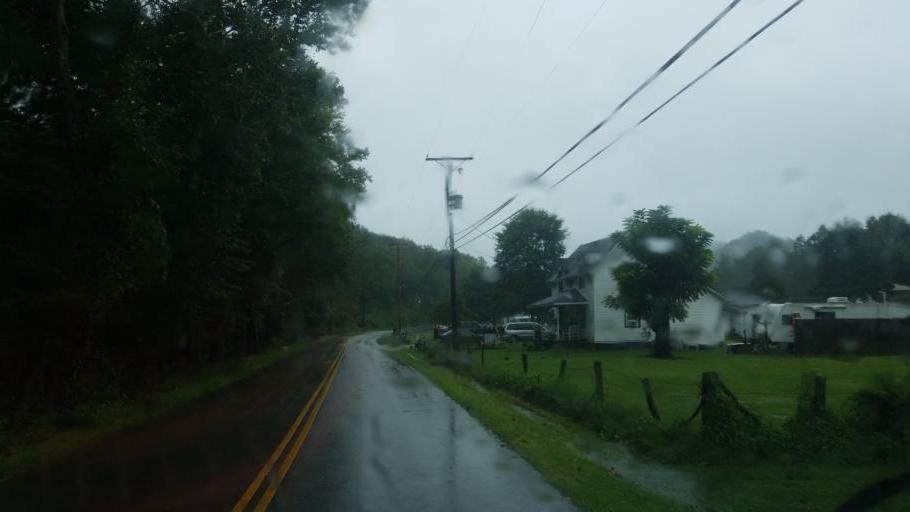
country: US
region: Ohio
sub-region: Scioto County
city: West Portsmouth
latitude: 38.7385
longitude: -83.0699
